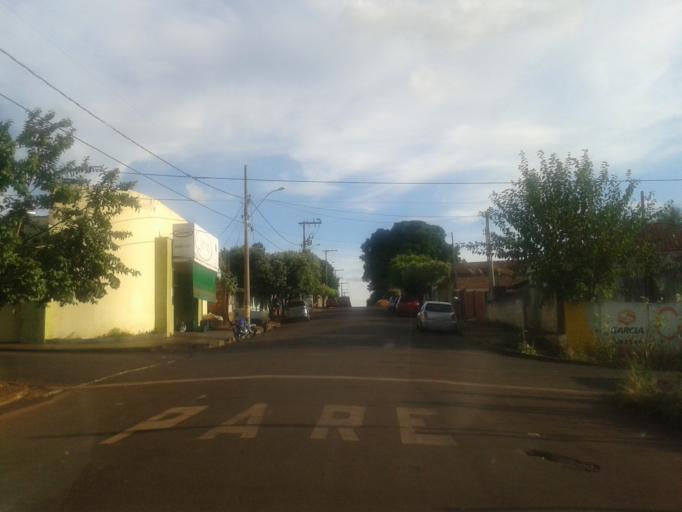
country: BR
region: Minas Gerais
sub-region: Capinopolis
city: Capinopolis
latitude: -18.6793
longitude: -49.5686
